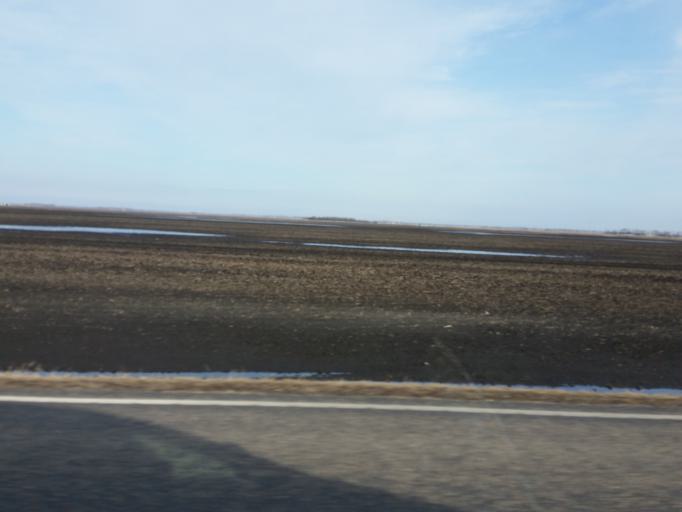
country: US
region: North Dakota
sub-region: Walsh County
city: Grafton
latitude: 48.4149
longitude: -97.2996
